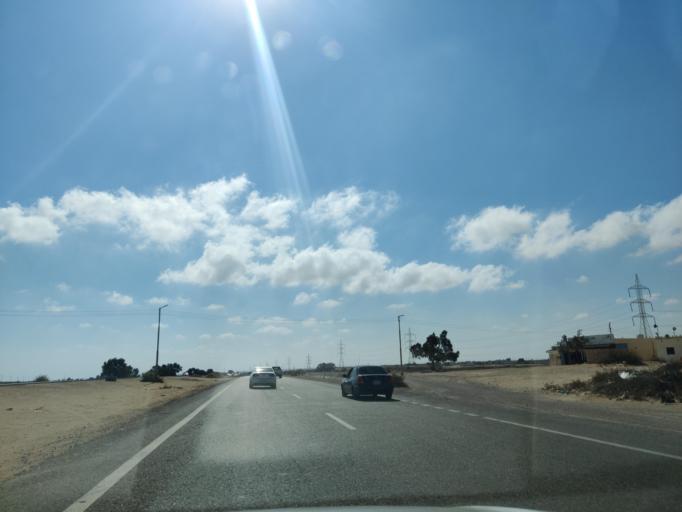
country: EG
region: Muhafazat Matruh
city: Al `Alamayn
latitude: 31.0540
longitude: 28.2813
